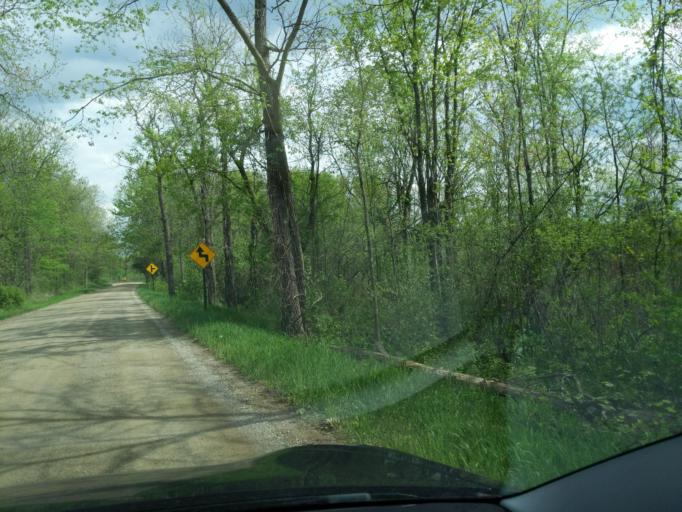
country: US
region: Michigan
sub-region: Washtenaw County
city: Chelsea
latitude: 42.4030
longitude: -84.0560
